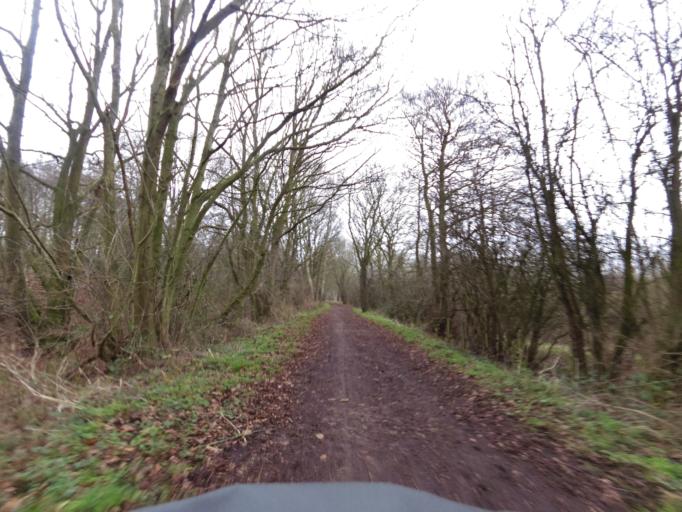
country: GB
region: England
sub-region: Norfolk
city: Mattishall
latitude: 52.7271
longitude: 1.1078
